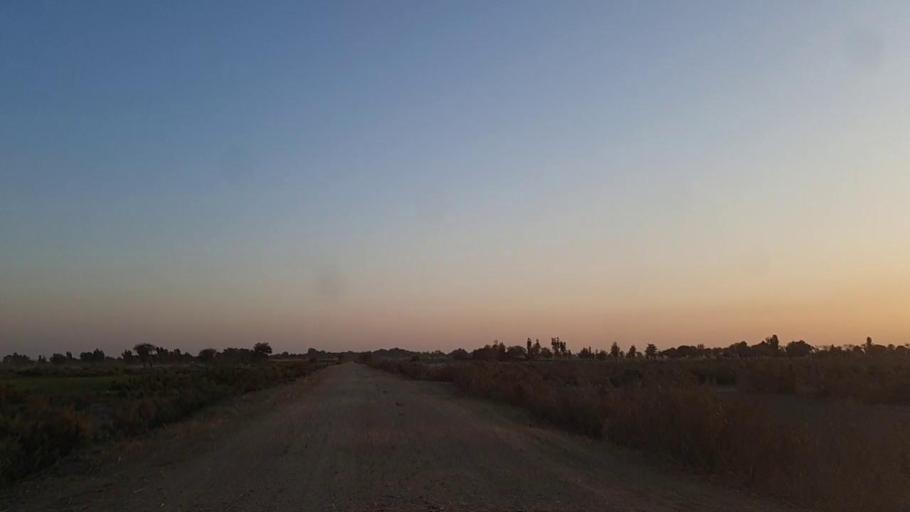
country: PK
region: Sindh
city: Samaro
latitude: 25.3160
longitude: 69.3693
